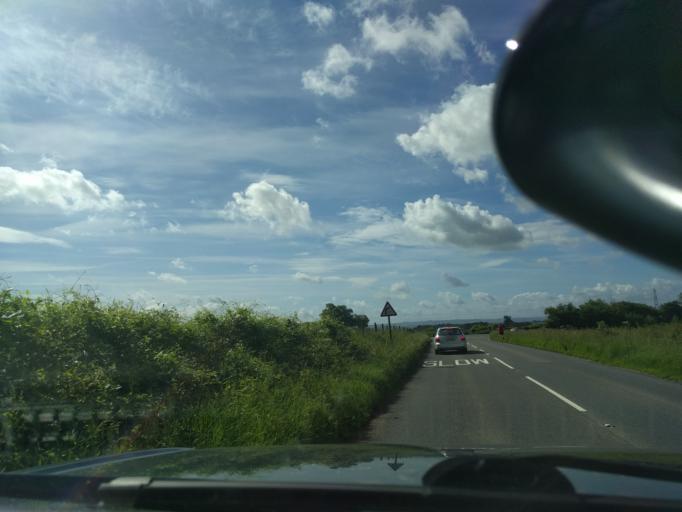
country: GB
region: England
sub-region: Wiltshire
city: Box
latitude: 51.4001
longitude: -2.2309
